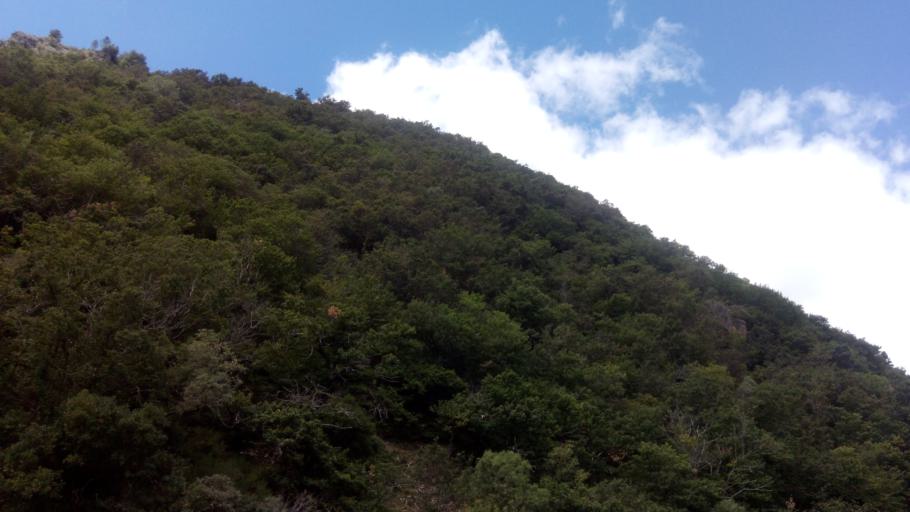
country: ES
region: Galicia
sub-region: Provincia de Lugo
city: Sober
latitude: 42.4009
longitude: -7.6293
